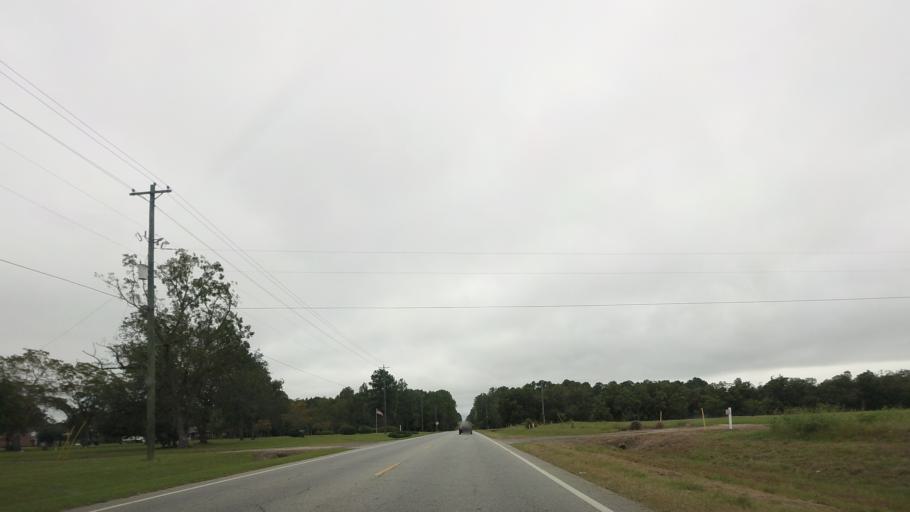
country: US
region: Georgia
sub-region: Berrien County
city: Ray City
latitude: 31.0085
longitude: -83.1983
